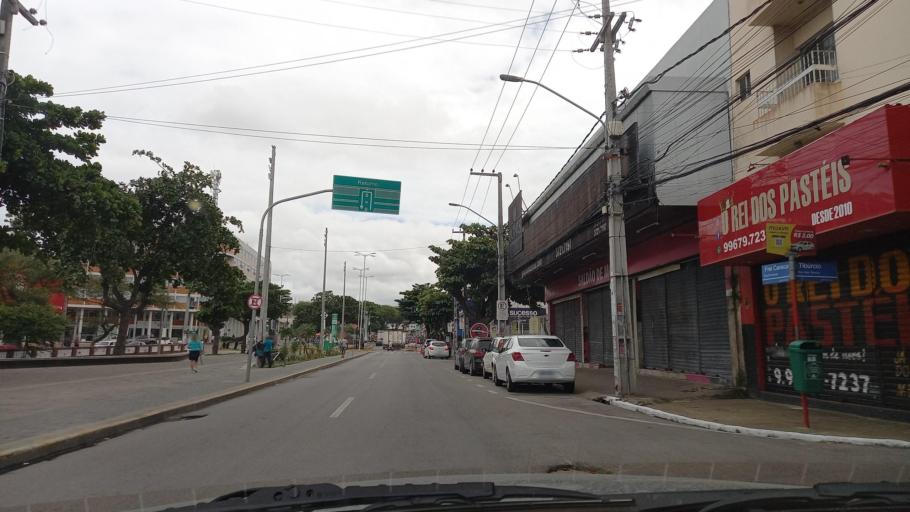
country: BR
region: Pernambuco
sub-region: Caruaru
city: Caruaru
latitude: -8.2824
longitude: -35.9704
